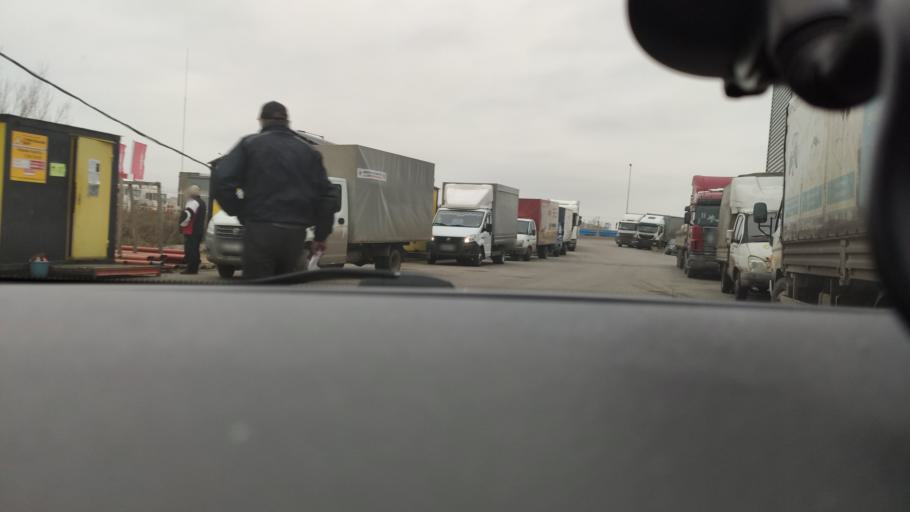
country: RU
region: Perm
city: Kondratovo
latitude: 57.9410
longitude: 56.1419
